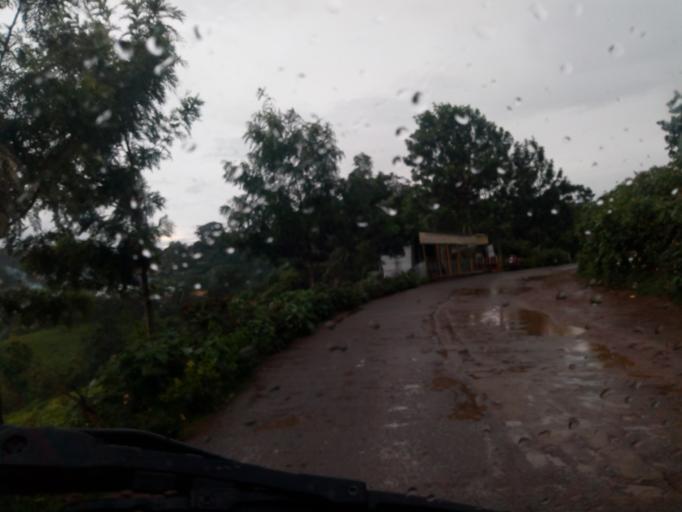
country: IN
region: Tamil Nadu
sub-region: Nilgiri
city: Wellington
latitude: 11.3486
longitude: 76.8140
